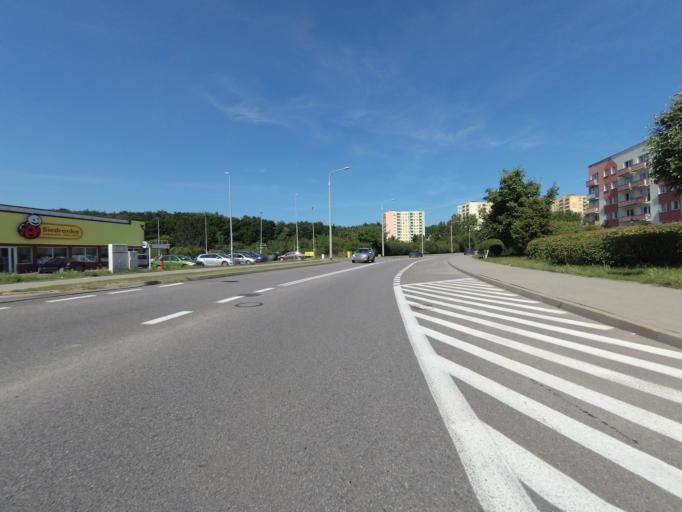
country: PL
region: Pomeranian Voivodeship
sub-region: Gdynia
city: Wielki Kack
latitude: 54.4919
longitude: 18.5095
